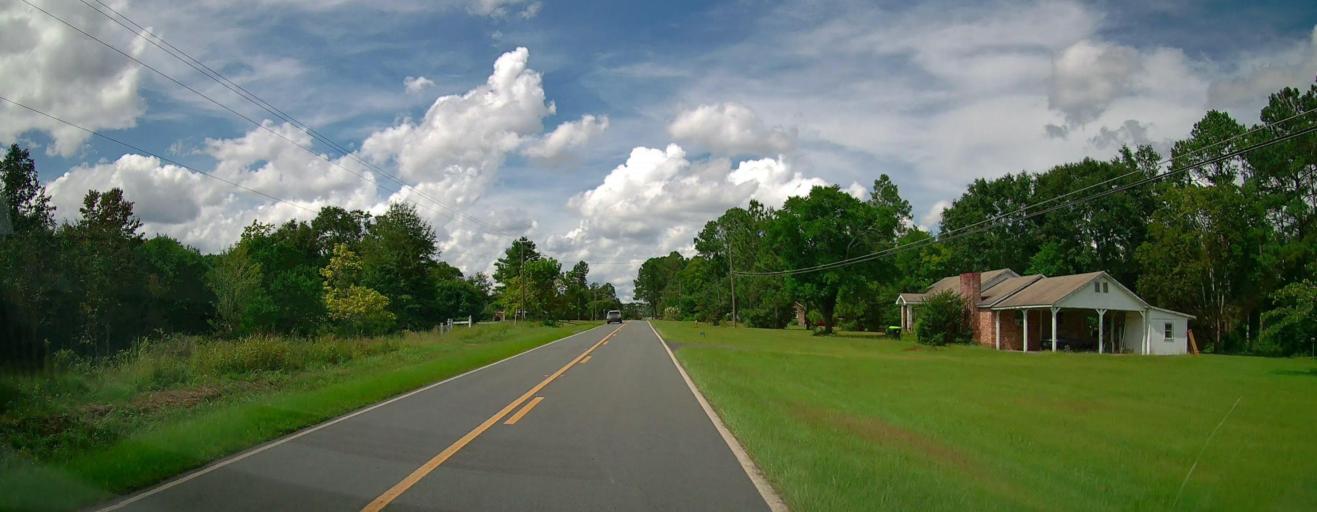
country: US
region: Georgia
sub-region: Taylor County
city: Butler
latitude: 32.5465
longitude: -84.2272
